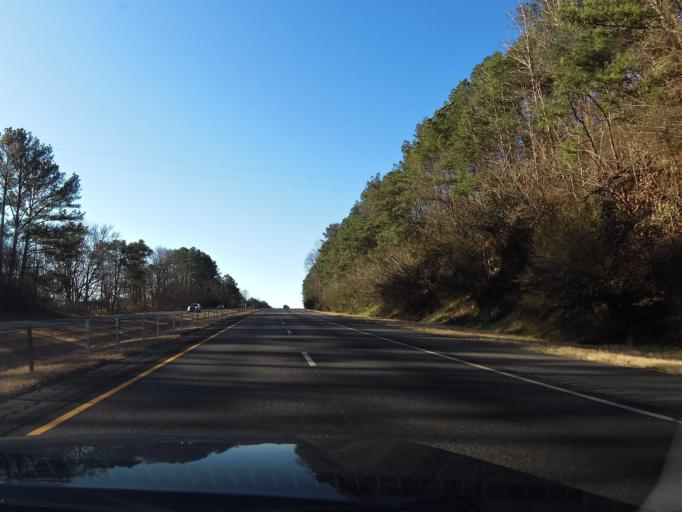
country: US
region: Alabama
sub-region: Blount County
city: Smoke Rise
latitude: 33.9775
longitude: -86.8609
